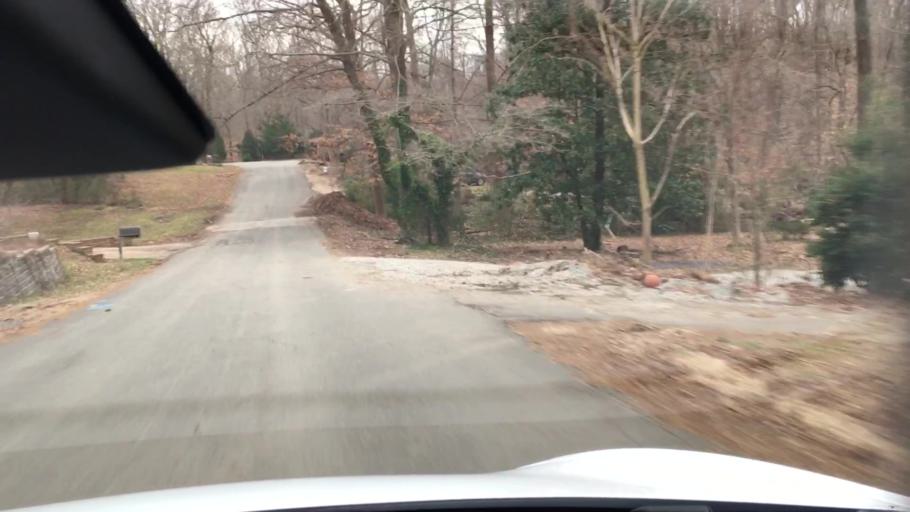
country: US
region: Virginia
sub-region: Chesterfield County
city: Bon Air
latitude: 37.5293
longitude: -77.5657
